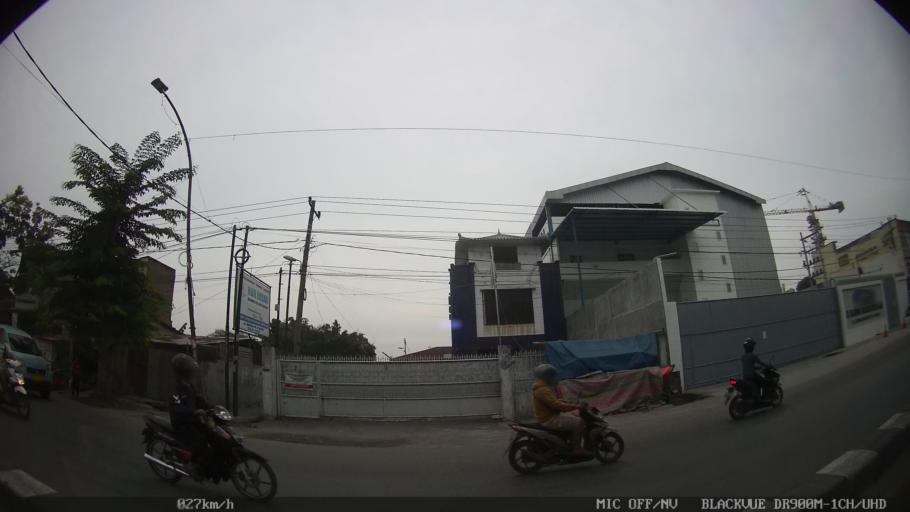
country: ID
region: North Sumatra
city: Medan
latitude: 3.5972
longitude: 98.7178
